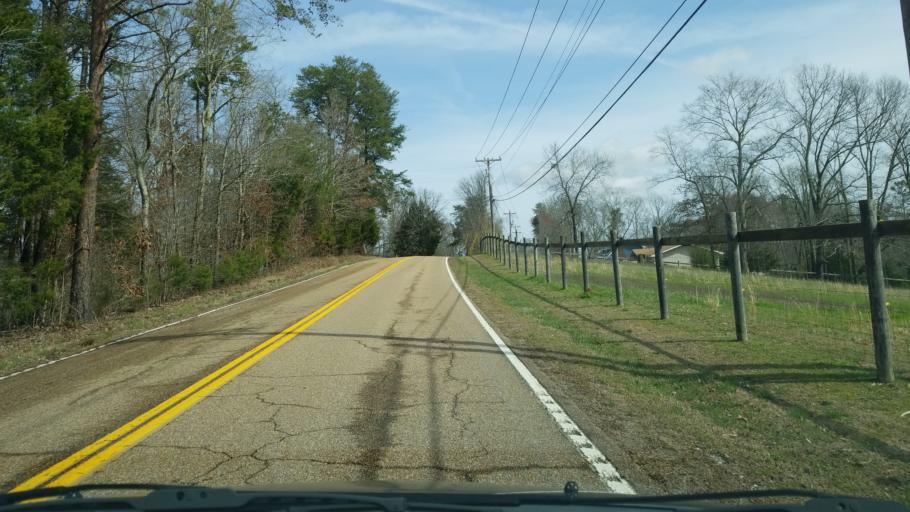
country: US
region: Tennessee
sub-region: Hamilton County
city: Lakesite
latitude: 35.1755
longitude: -85.0530
